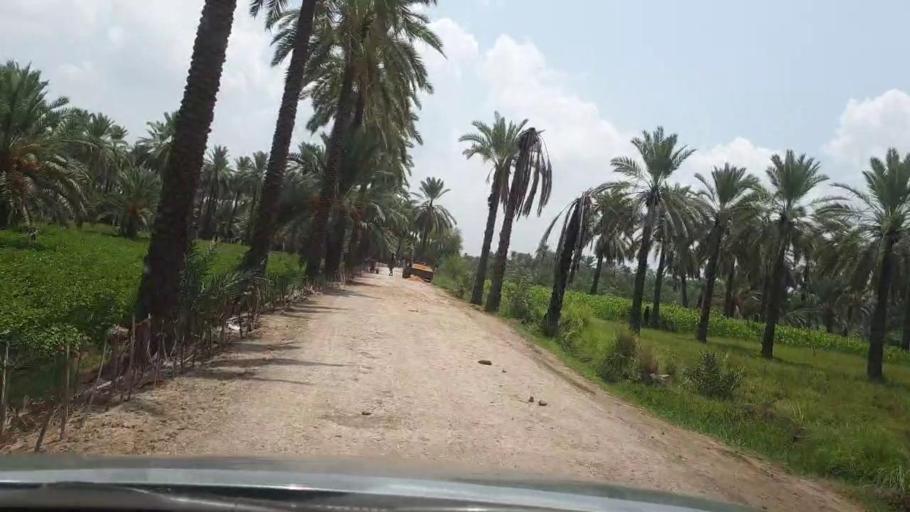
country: PK
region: Sindh
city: Khairpur
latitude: 27.6304
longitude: 68.7370
